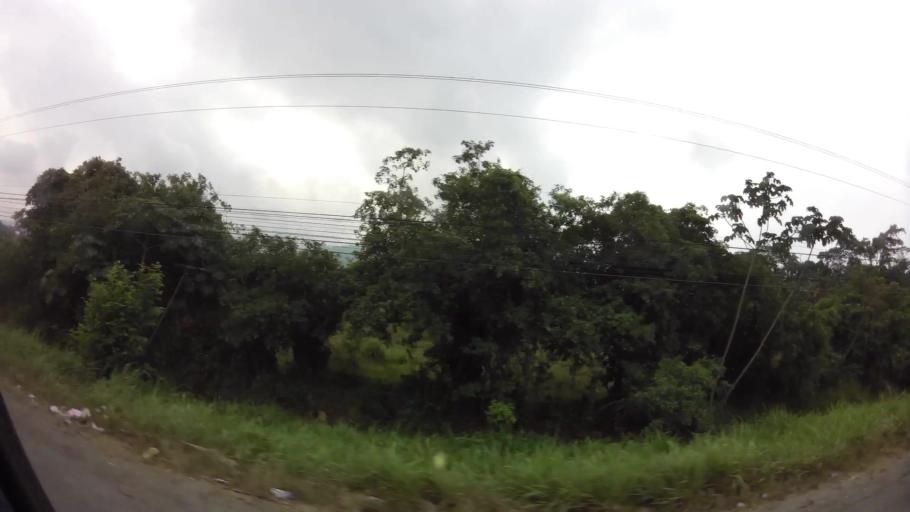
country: HN
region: Yoro
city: El Progreso
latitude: 15.4412
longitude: -87.7920
